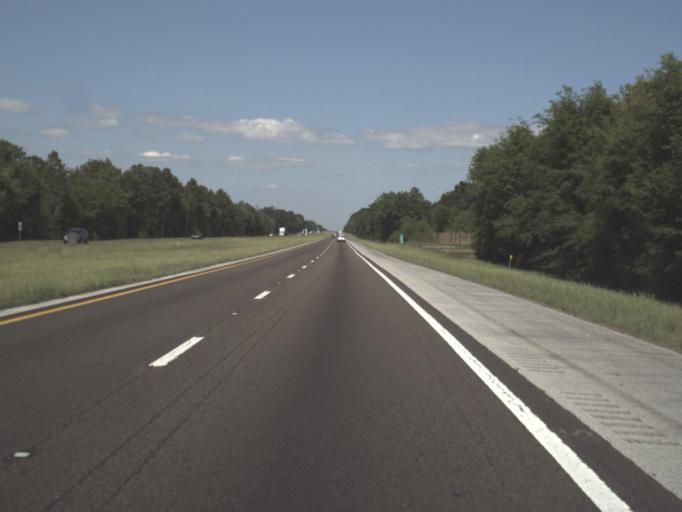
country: US
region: Florida
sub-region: Santa Rosa County
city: East Milton
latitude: 30.6277
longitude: -86.9362
